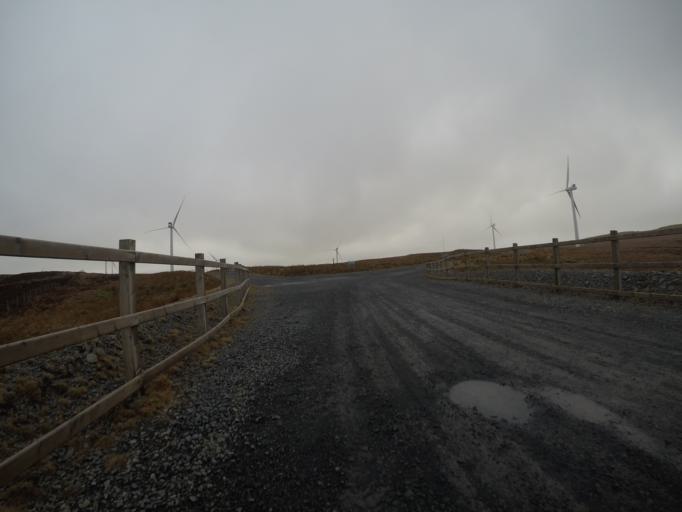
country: GB
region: Scotland
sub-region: North Ayrshire
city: Fairlie
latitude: 55.7539
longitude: -4.7959
